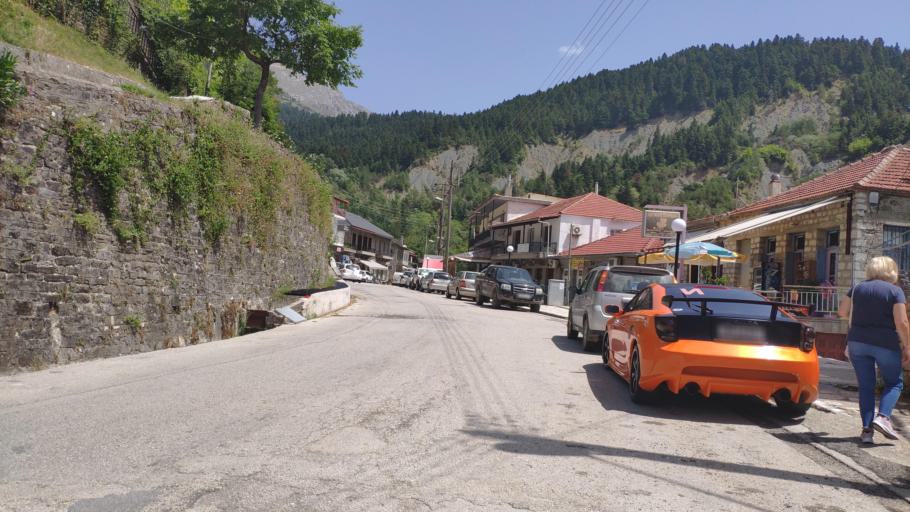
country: GR
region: Epirus
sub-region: Nomos Artas
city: Voulgareli
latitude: 39.3705
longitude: 21.1837
